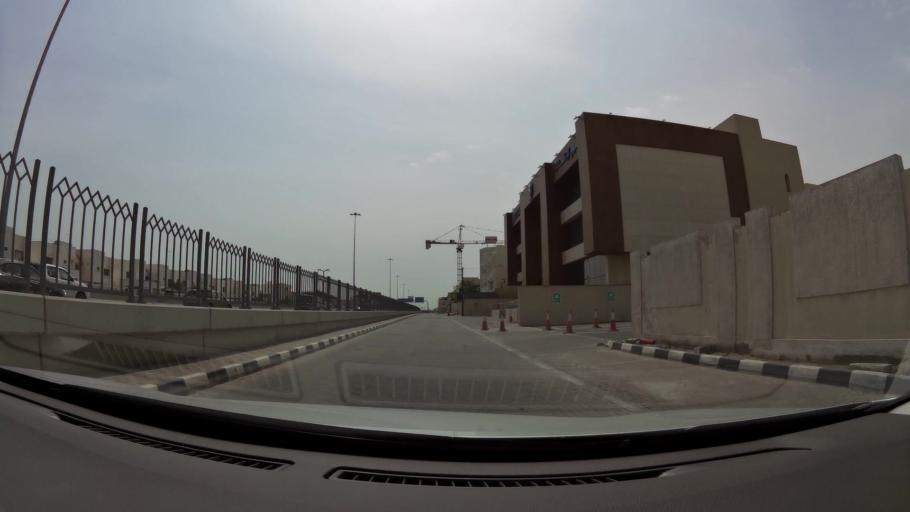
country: QA
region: Baladiyat ad Dawhah
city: Doha
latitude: 25.2697
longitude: 51.4927
